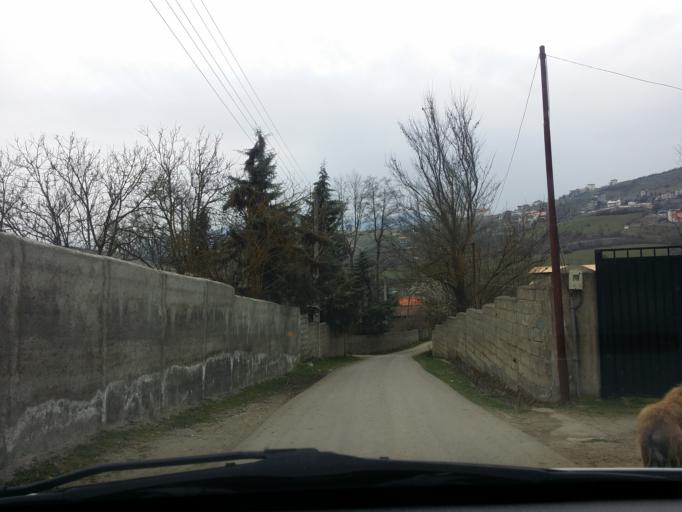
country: IR
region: Mazandaran
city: `Abbasabad
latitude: 36.5477
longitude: 51.1662
